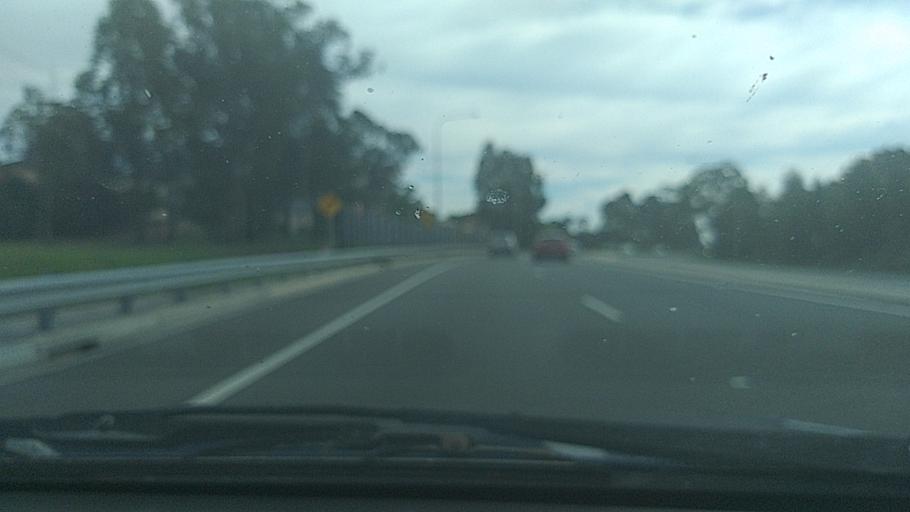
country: AU
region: New South Wales
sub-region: Penrith Municipality
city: Werrington Downs
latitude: -33.7217
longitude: 150.7225
